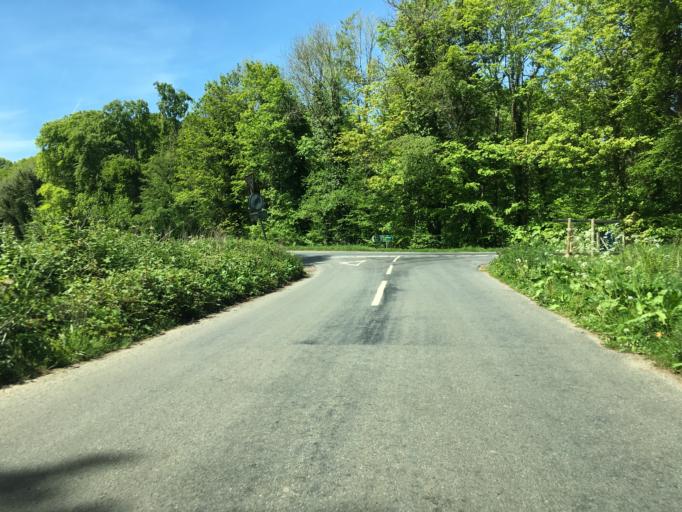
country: GB
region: England
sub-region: Gloucestershire
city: Coates
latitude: 51.7158
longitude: -2.0530
